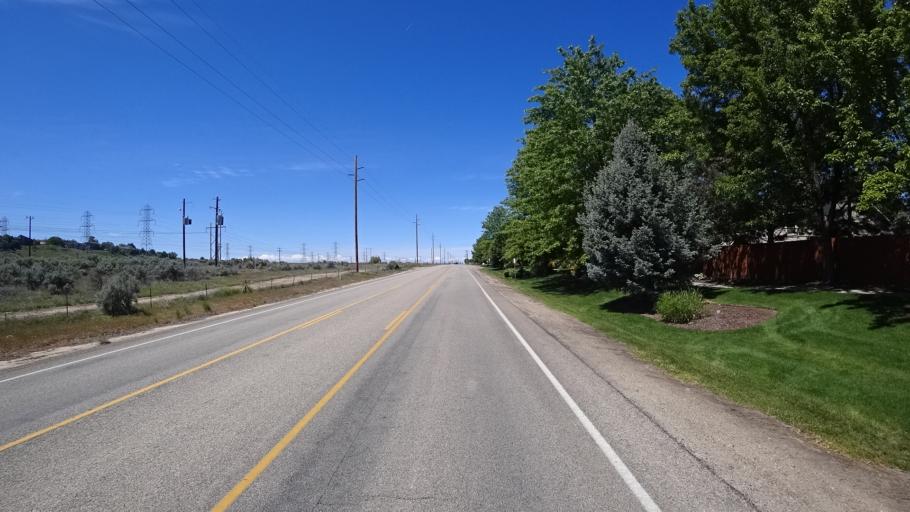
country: US
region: Idaho
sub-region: Ada County
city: Boise
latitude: 43.5600
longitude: -116.1396
